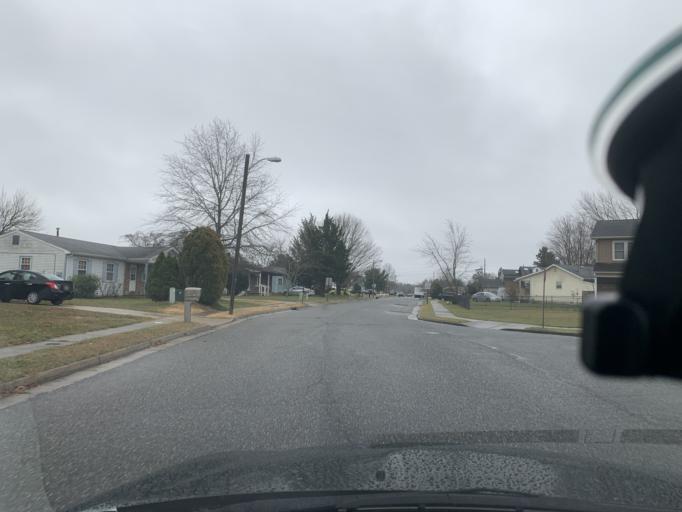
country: US
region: New Jersey
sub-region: Atlantic County
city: Pomona
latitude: 39.4309
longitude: -74.5905
